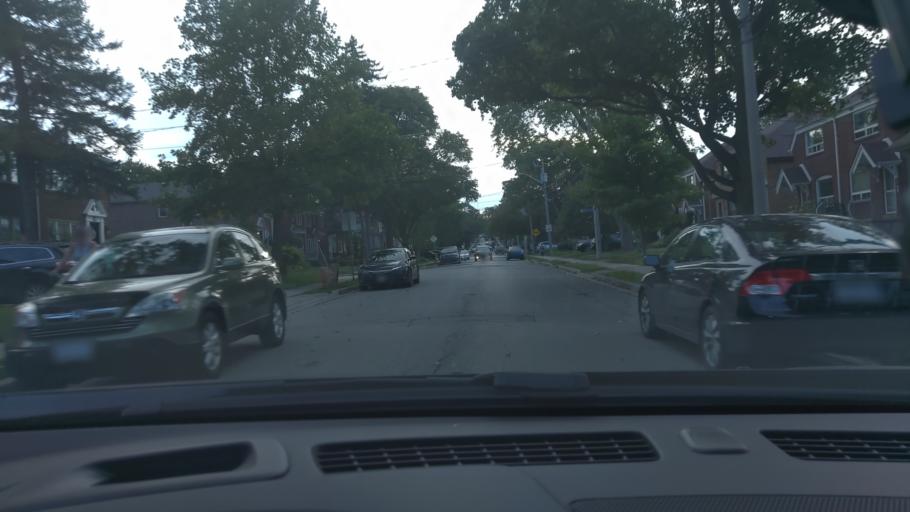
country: CA
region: Ontario
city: Toronto
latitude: 43.7178
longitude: -79.3699
